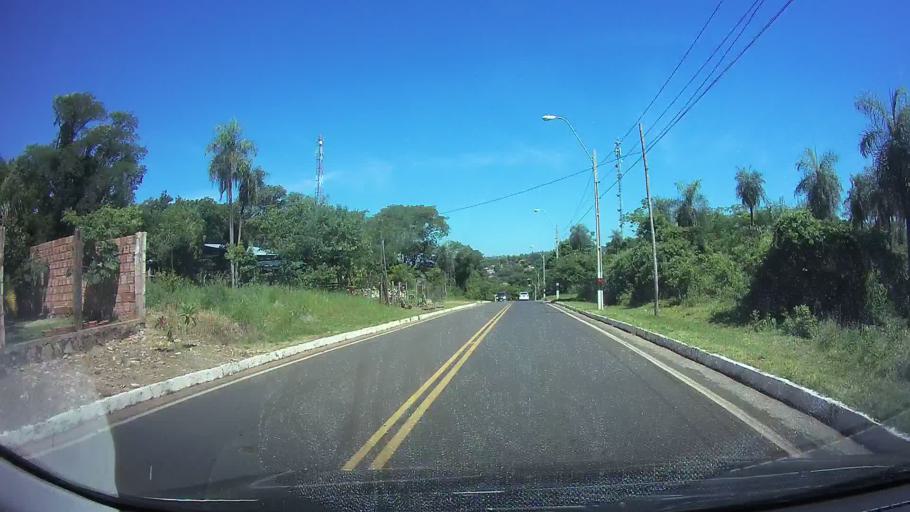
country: PY
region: Central
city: Aregua
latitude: -25.3097
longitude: -57.3960
